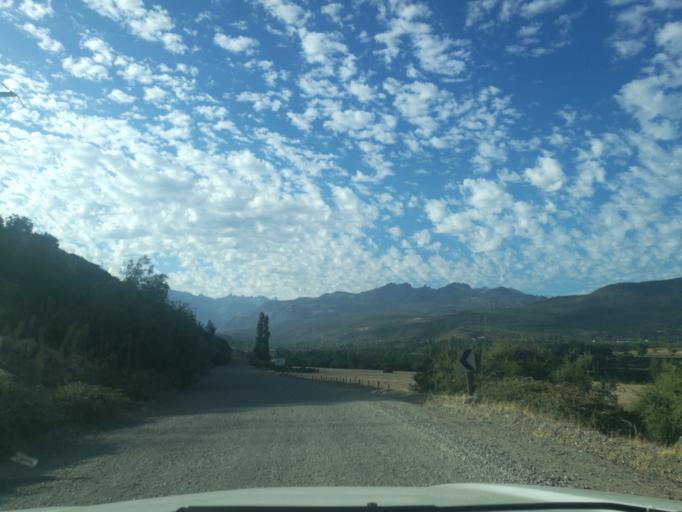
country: CL
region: O'Higgins
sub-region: Provincia de Cachapoal
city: Machali
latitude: -34.2372
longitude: -70.4743
